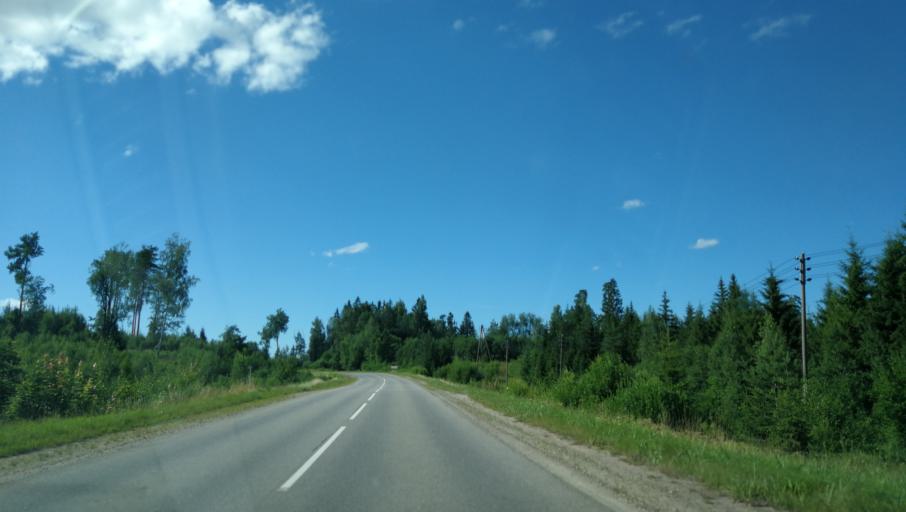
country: LV
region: Madonas Rajons
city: Madona
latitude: 56.8791
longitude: 26.1750
